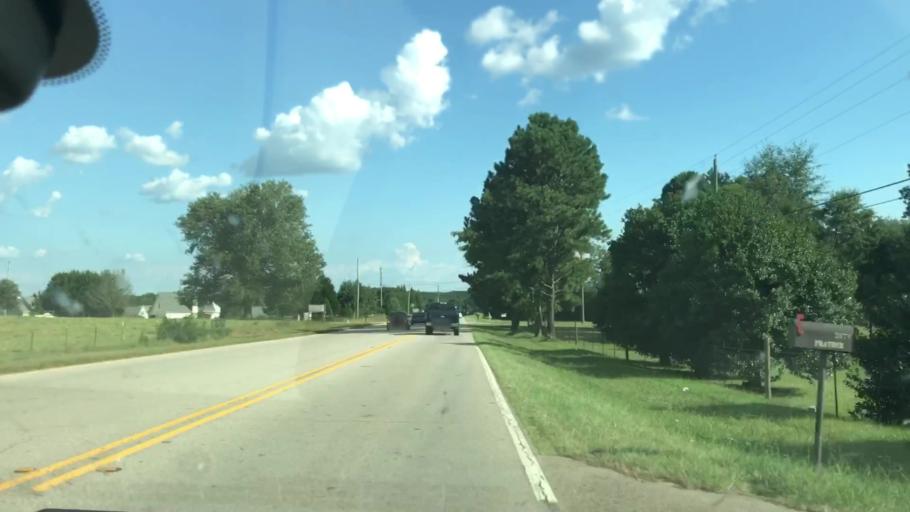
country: US
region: Georgia
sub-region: Troup County
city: La Grange
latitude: 32.9769
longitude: -84.9903
